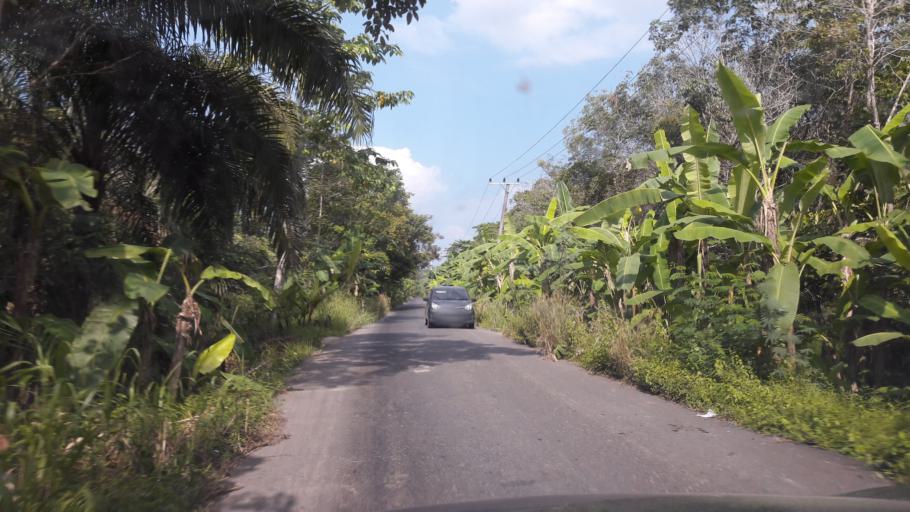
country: ID
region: South Sumatra
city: Prabumulih
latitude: -3.3143
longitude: 104.1960
